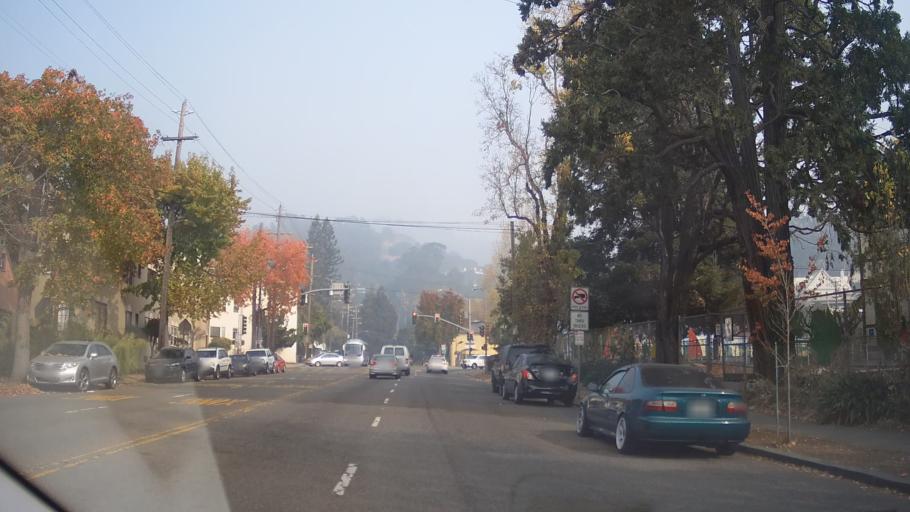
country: US
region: California
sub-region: Alameda County
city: Berkeley
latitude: 37.8573
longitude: -122.2459
